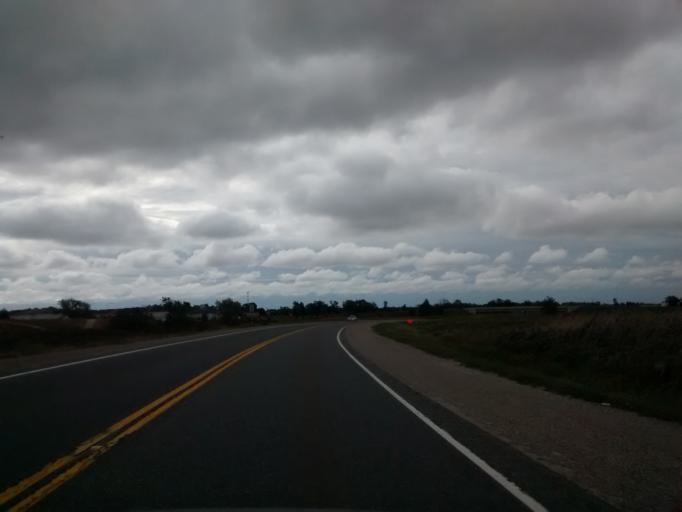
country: CA
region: Ontario
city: Ancaster
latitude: 43.1514
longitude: -79.9276
